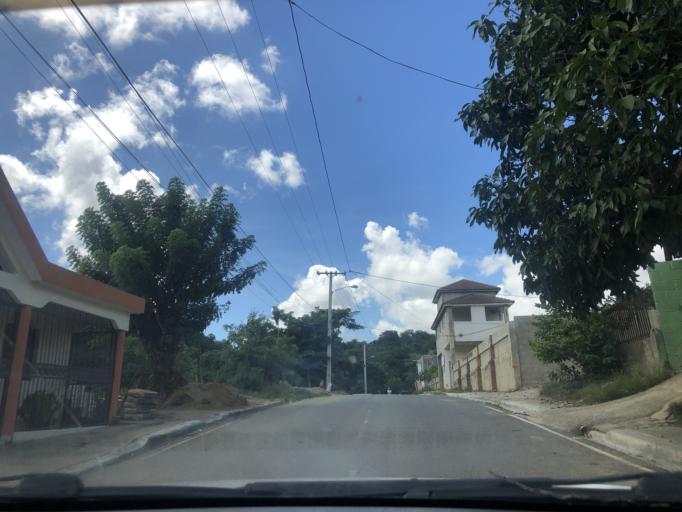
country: DO
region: Santiago
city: Santiago de los Caballeros
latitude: 19.4096
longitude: -70.7040
